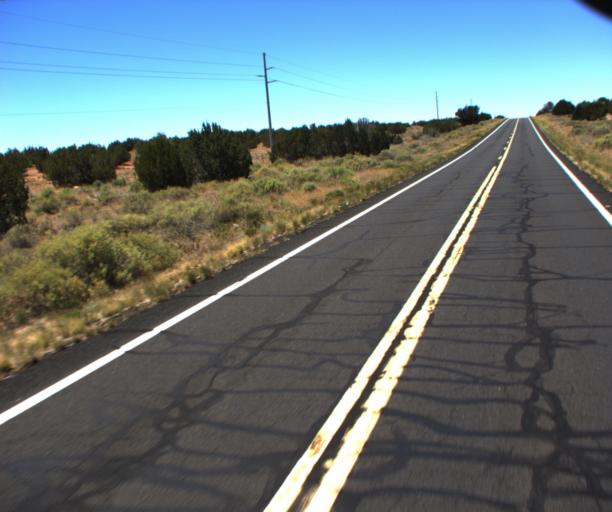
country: US
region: Arizona
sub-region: Coconino County
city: LeChee
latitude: 34.8376
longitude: -110.9431
